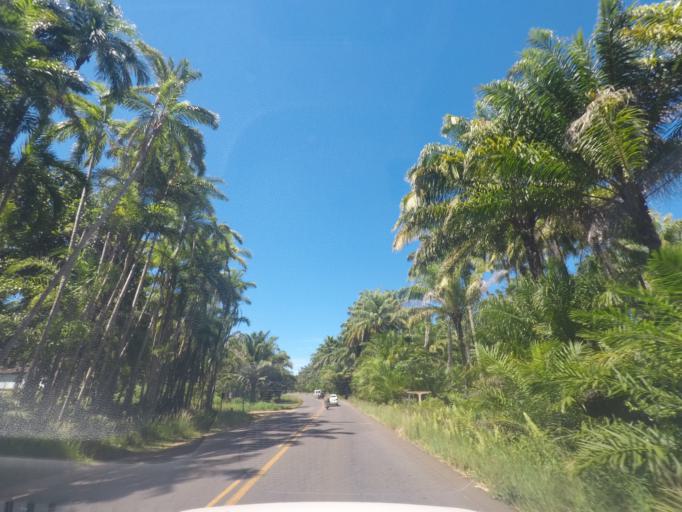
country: BR
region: Bahia
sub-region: Taperoa
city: Taperoa
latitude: -13.4683
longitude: -39.0879
